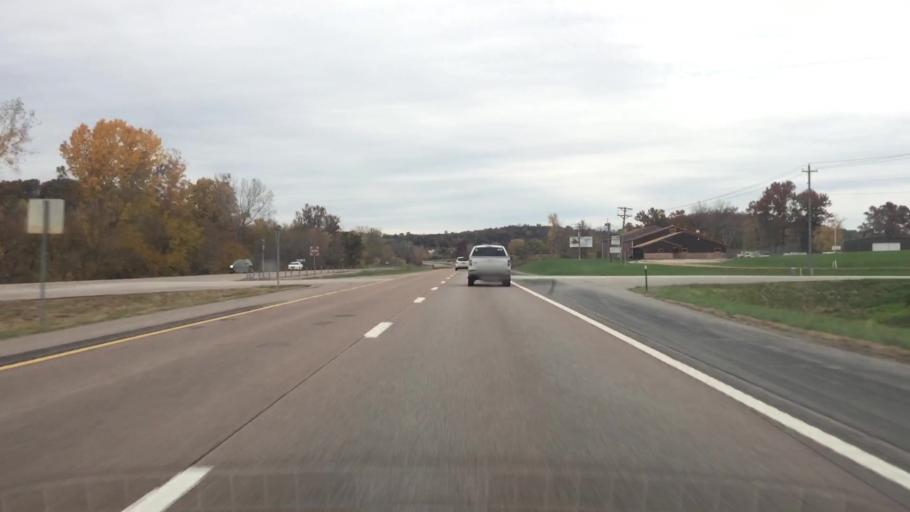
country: US
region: Missouri
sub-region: Cole County
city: Jefferson City
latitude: 38.6425
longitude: -92.1998
